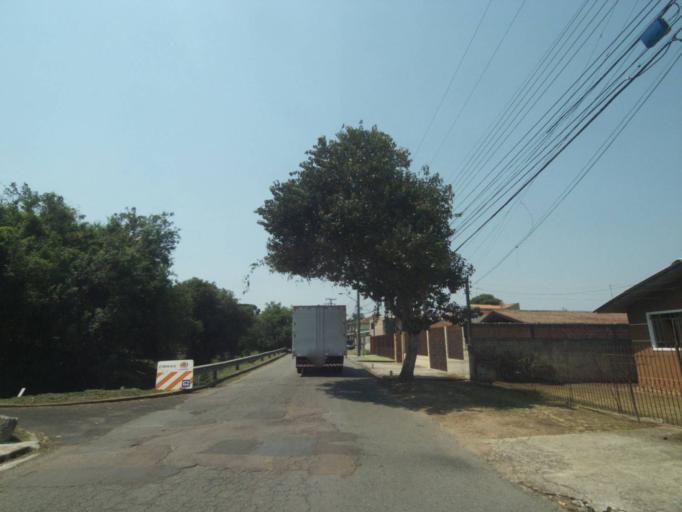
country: BR
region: Parana
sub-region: Sao Jose Dos Pinhais
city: Sao Jose dos Pinhais
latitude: -25.5102
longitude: -49.2710
